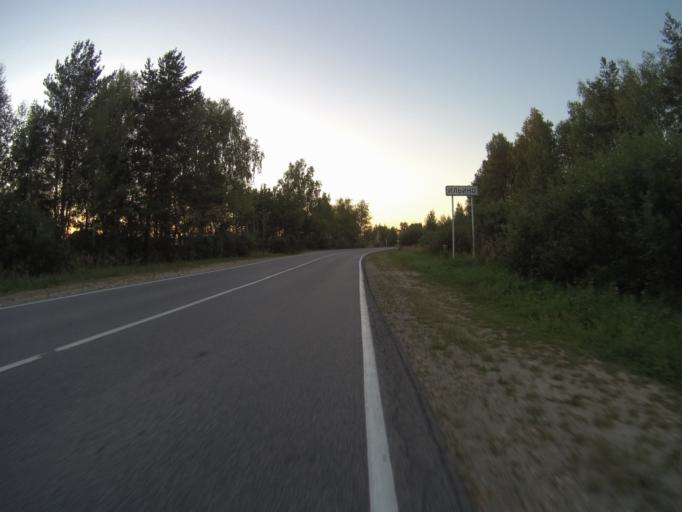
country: RU
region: Vladimir
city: Golovino
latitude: 55.9104
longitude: 40.6075
